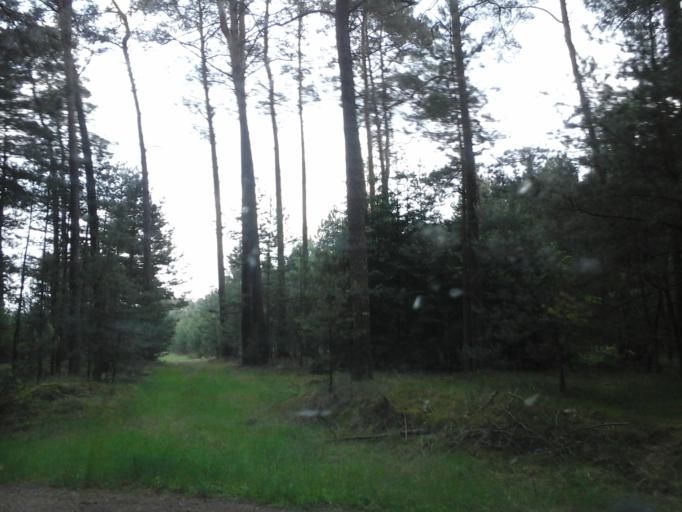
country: PL
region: West Pomeranian Voivodeship
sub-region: Powiat drawski
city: Kalisz Pomorski
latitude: 53.2094
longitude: 15.9029
